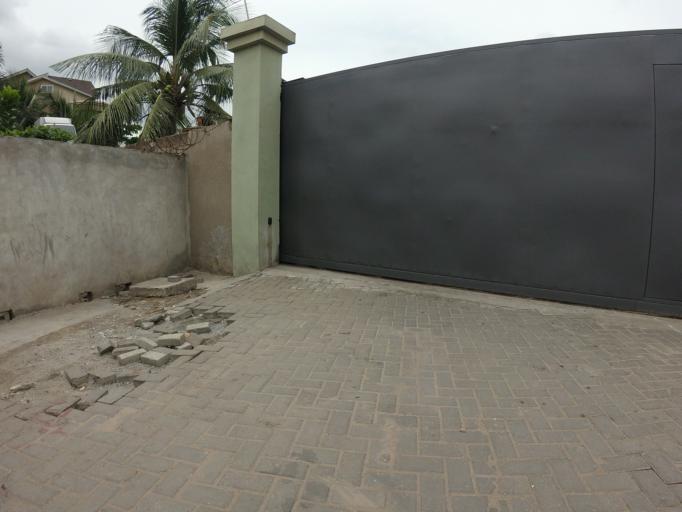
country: GH
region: Greater Accra
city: Dome
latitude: 5.6007
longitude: -0.2235
